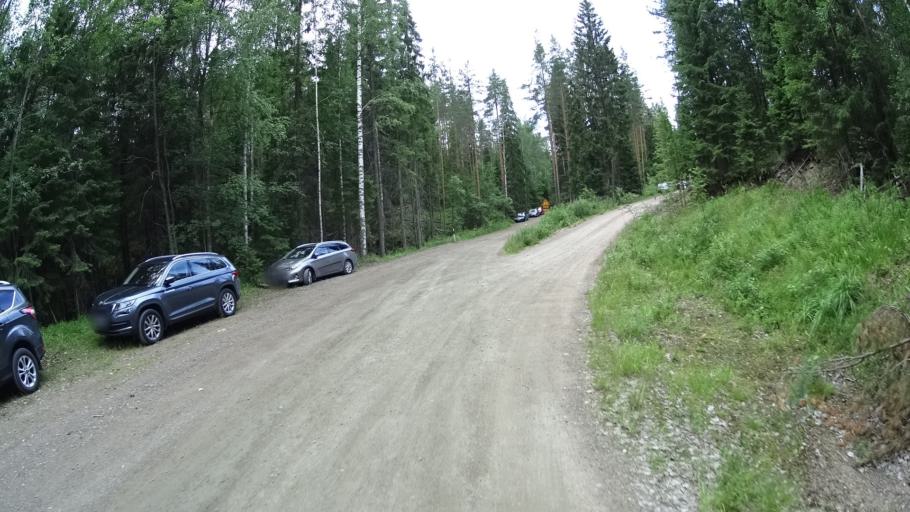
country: FI
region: Southern Savonia
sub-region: Mikkeli
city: Maentyharju
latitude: 61.1551
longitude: 26.8868
